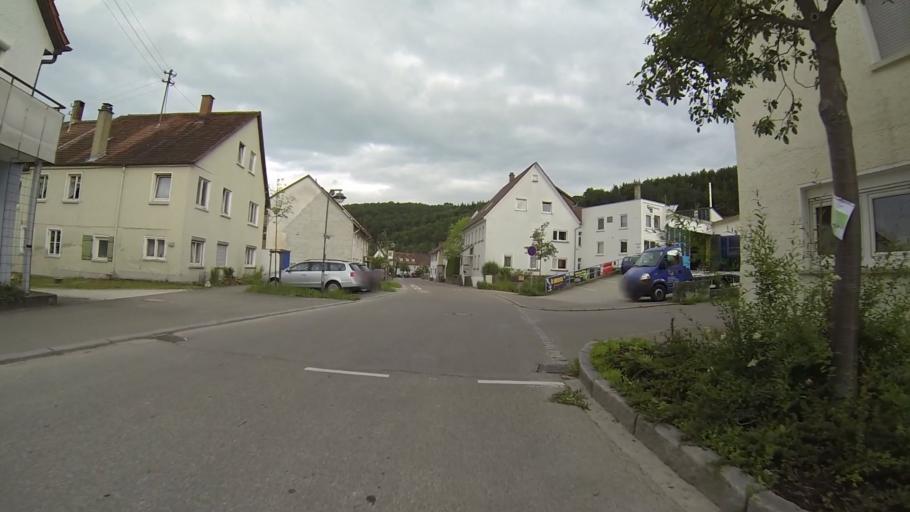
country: DE
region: Baden-Wuerttemberg
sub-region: Tuebingen Region
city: Blaubeuren
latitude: 48.3984
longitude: 9.8023
